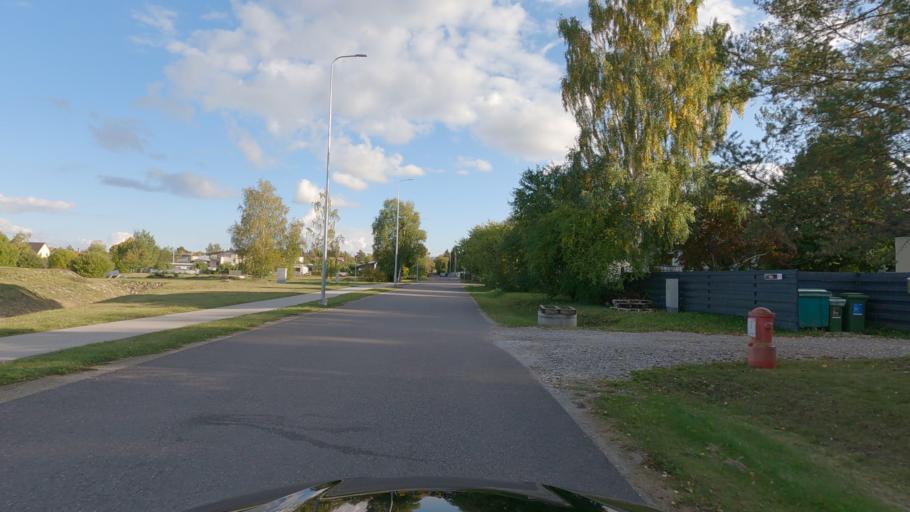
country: EE
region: Harju
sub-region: Saku vald
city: Saku
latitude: 59.3027
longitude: 24.6511
